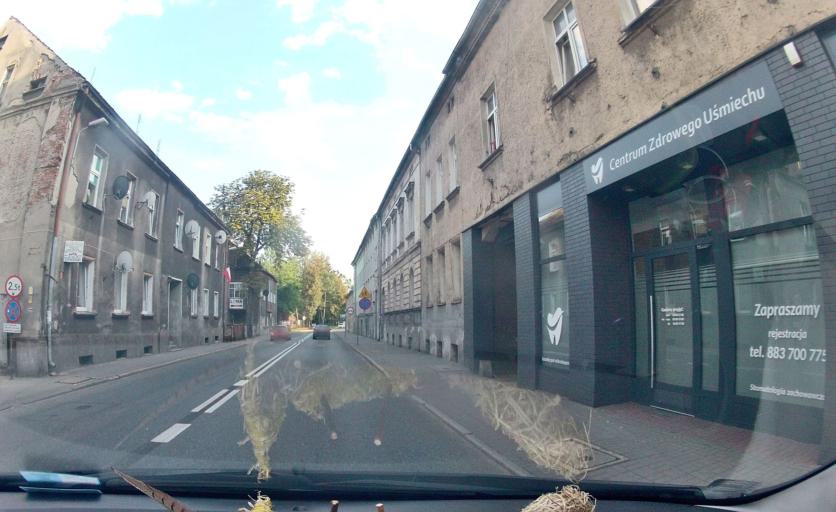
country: PL
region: Opole Voivodeship
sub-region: Powiat kluczborski
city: Kluczbork
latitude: 50.9721
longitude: 18.2180
